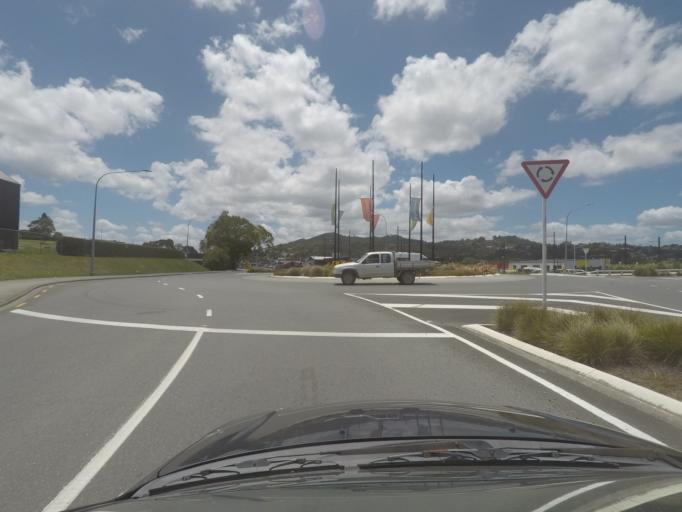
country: NZ
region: Northland
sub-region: Whangarei
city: Whangarei
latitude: -35.7353
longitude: 174.3331
